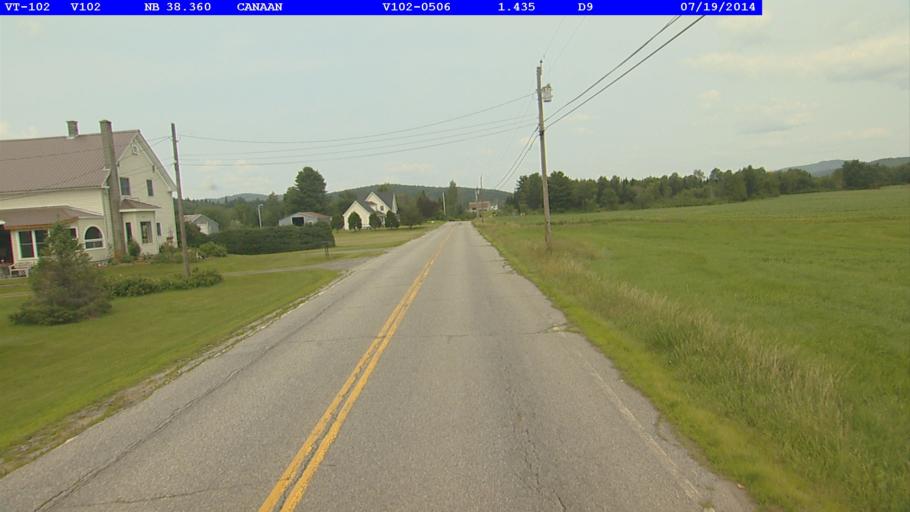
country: US
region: New Hampshire
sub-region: Coos County
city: Colebrook
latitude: 44.9276
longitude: -71.5231
